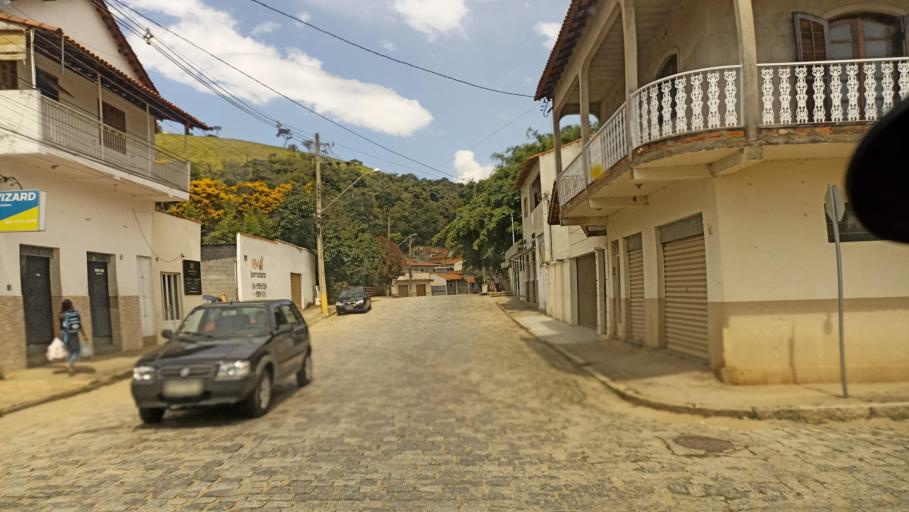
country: BR
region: Minas Gerais
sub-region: Passa Quatro
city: Passa Quatro
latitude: -22.3921
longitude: -44.9646
